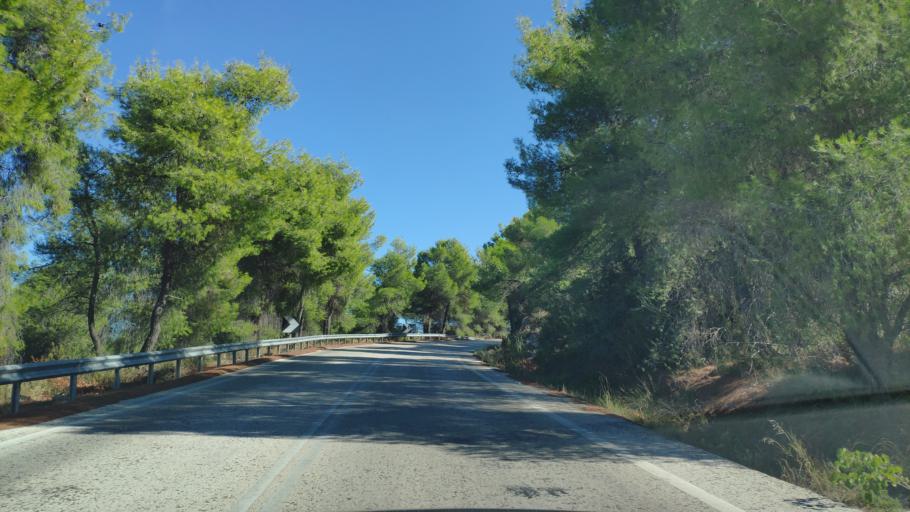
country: GR
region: Peloponnese
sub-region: Nomos Korinthias
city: Sofikon
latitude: 37.8288
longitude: 23.0504
